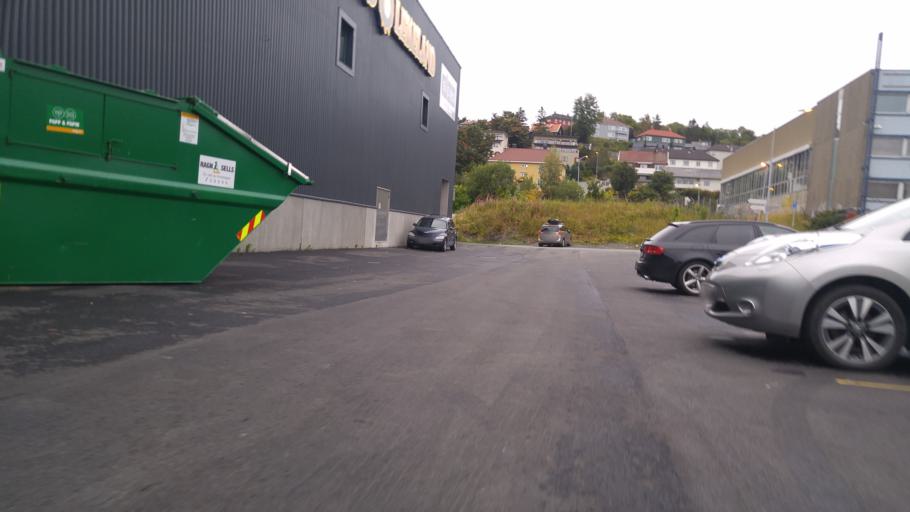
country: NO
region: Sor-Trondelag
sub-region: Trondheim
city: Trondheim
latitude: 63.4434
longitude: 10.4319
